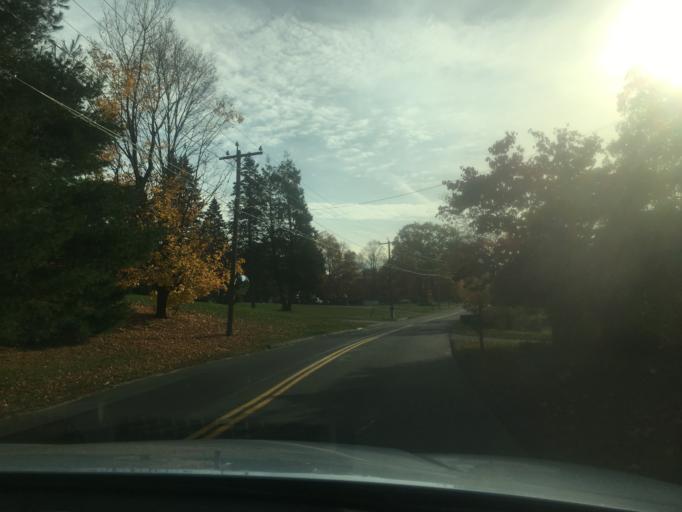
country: US
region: Connecticut
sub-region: Hartford County
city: Broad Brook
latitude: 41.8683
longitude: -72.5717
